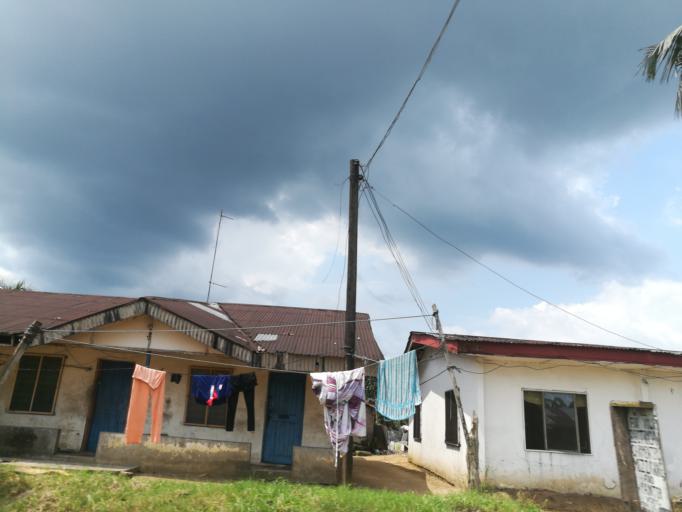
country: NG
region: Rivers
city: Okrika
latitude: 4.7286
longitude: 7.1525
